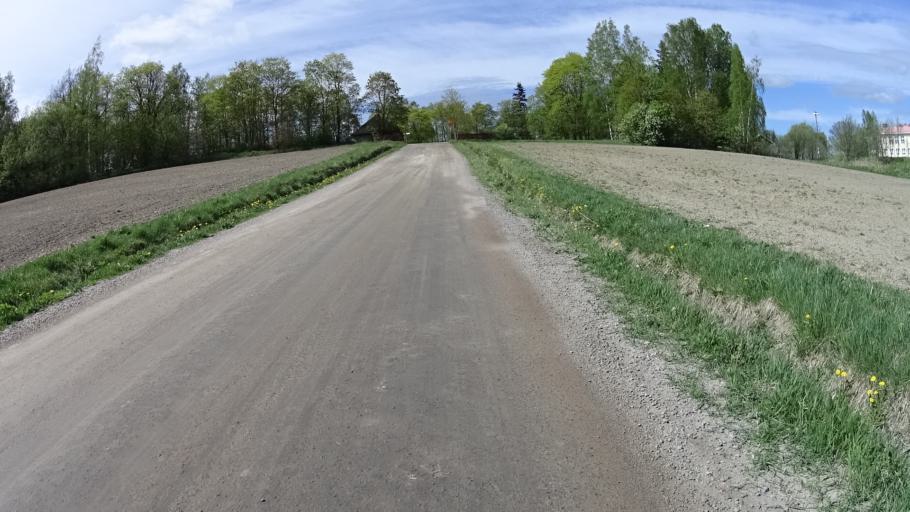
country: FI
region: Uusimaa
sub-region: Helsinki
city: Kilo
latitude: 60.2635
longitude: 24.7849
